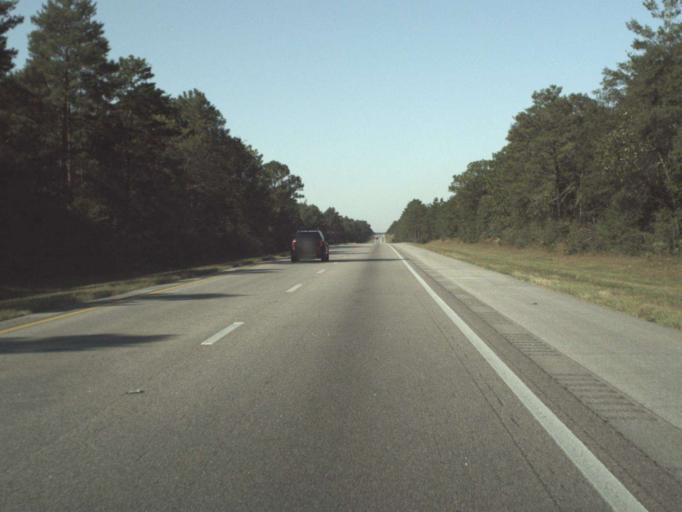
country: US
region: Florida
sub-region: Okaloosa County
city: Crestview
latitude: 30.7269
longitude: -86.4028
